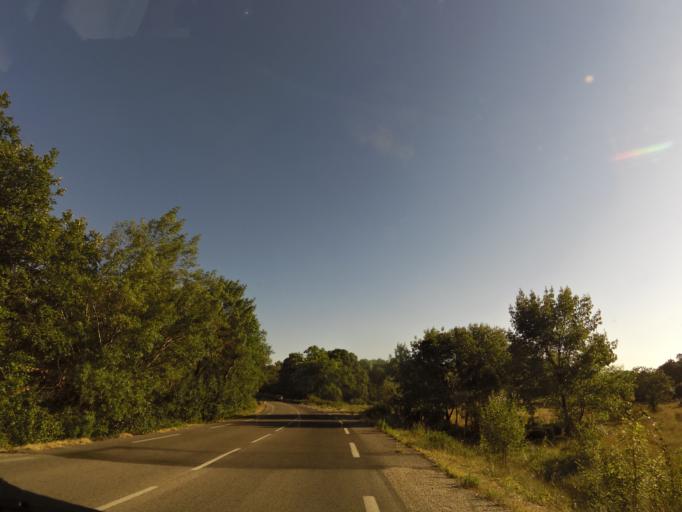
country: FR
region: Languedoc-Roussillon
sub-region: Departement du Gard
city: Quissac
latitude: 43.8823
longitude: 4.0075
